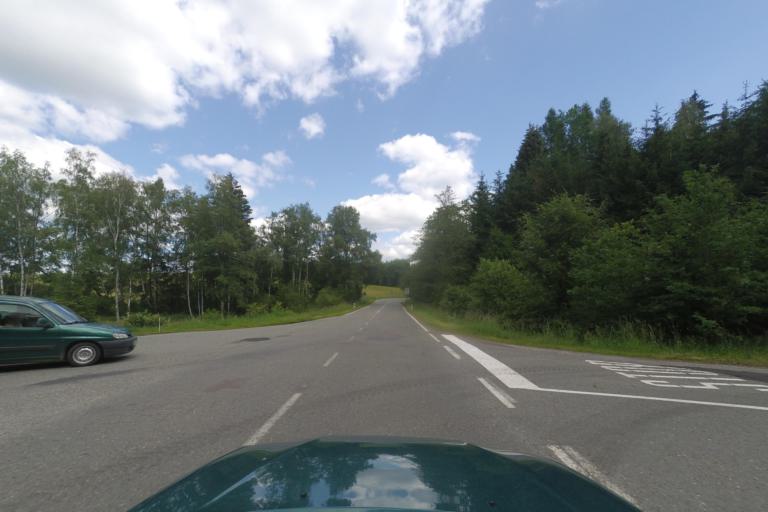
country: PL
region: Lower Silesian Voivodeship
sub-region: Powiat klodzki
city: Lewin Klodzki
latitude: 50.3464
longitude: 16.2338
